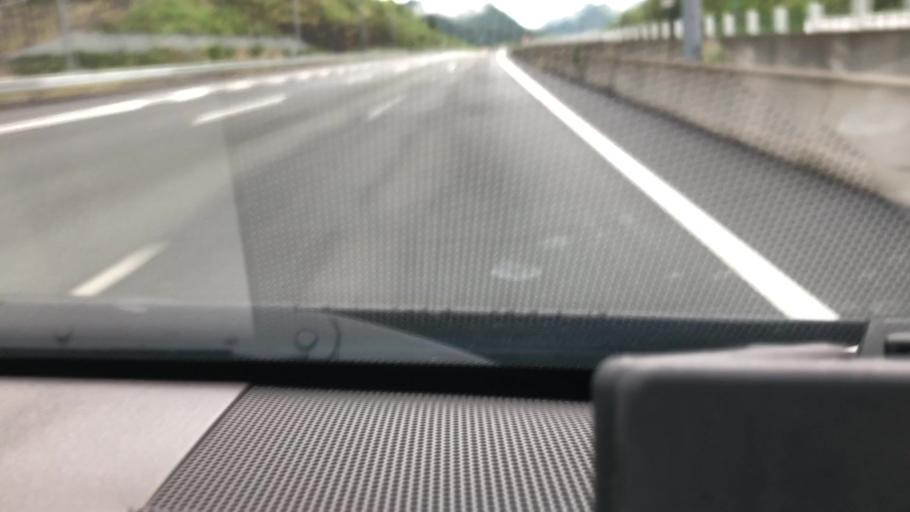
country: JP
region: Shizuoka
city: Fujieda
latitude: 34.9092
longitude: 138.2530
